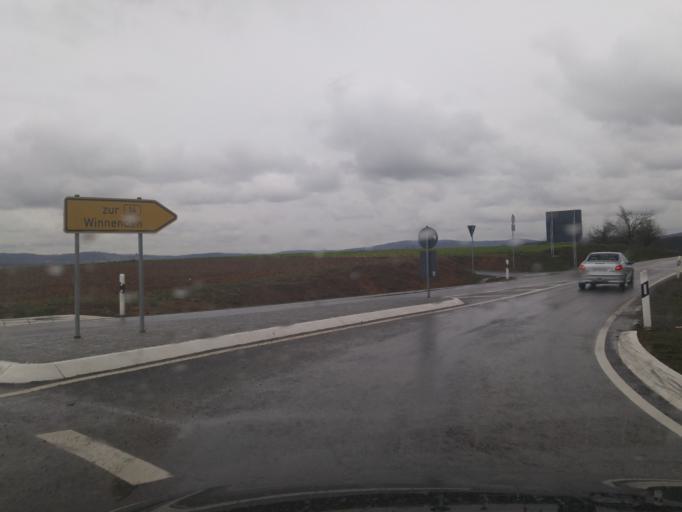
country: DE
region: Baden-Wuerttemberg
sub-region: Regierungsbezirk Stuttgart
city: Affalterbach
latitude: 48.9163
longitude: 9.3330
